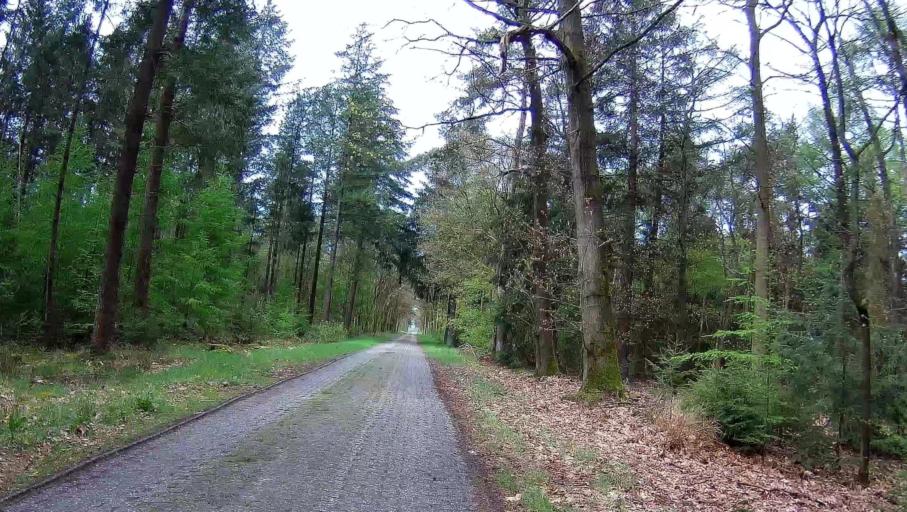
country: NL
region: Drenthe
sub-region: Gemeente Borger-Odoorn
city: Borger
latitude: 52.9717
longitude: 6.7322
